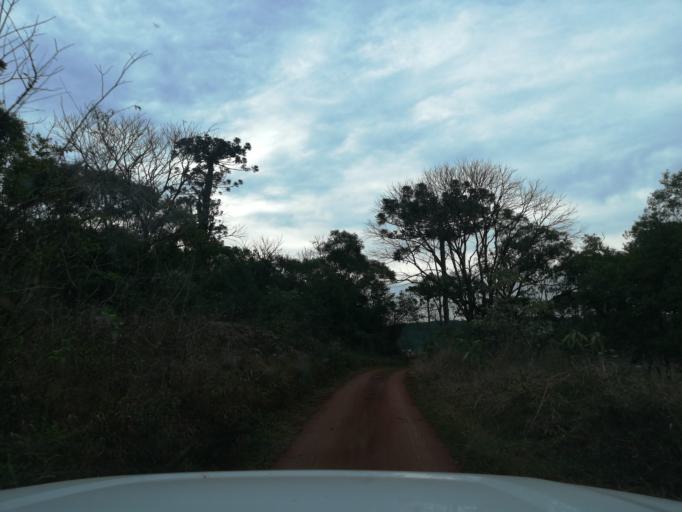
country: AR
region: Misiones
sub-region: Departamento de San Pedro
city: San Pedro
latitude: -26.6316
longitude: -54.0948
